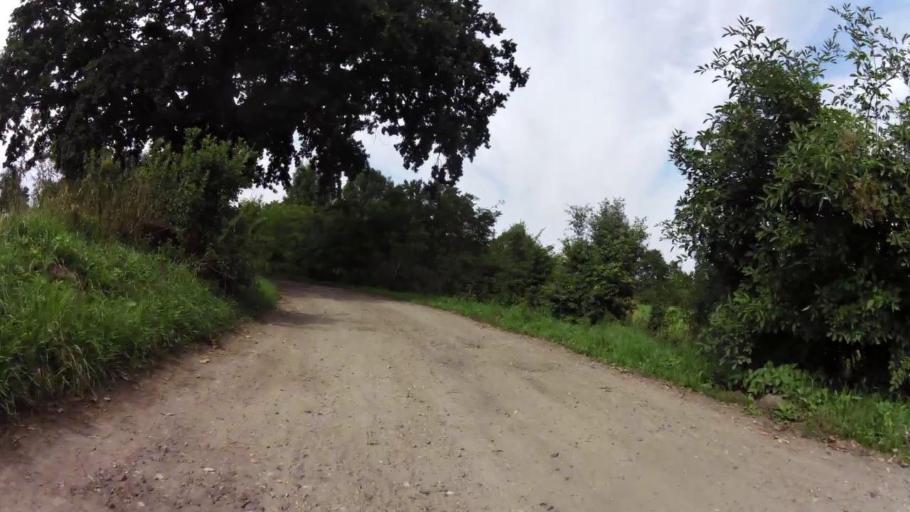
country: PL
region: West Pomeranian Voivodeship
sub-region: Powiat lobeski
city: Wegorzyno
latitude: 53.5347
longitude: 15.6133
